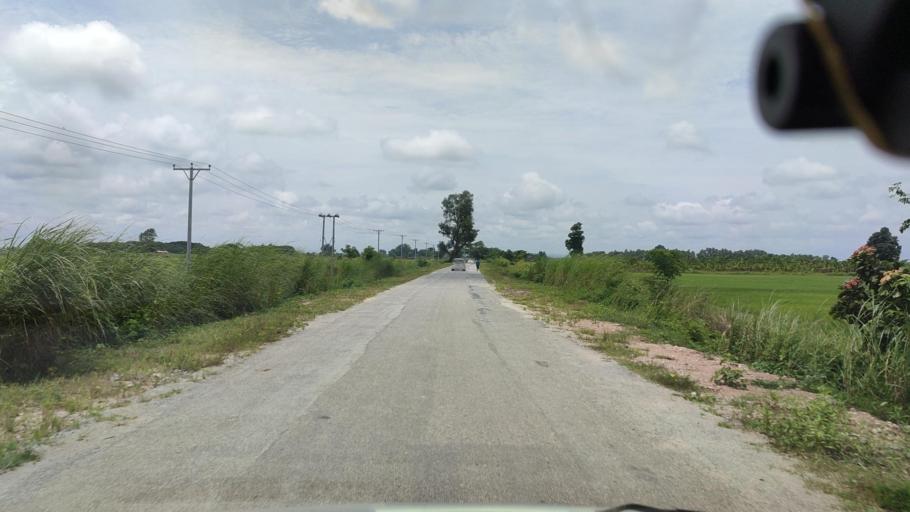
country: MM
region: Bago
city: Taungoo
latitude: 19.1515
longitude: 96.4104
